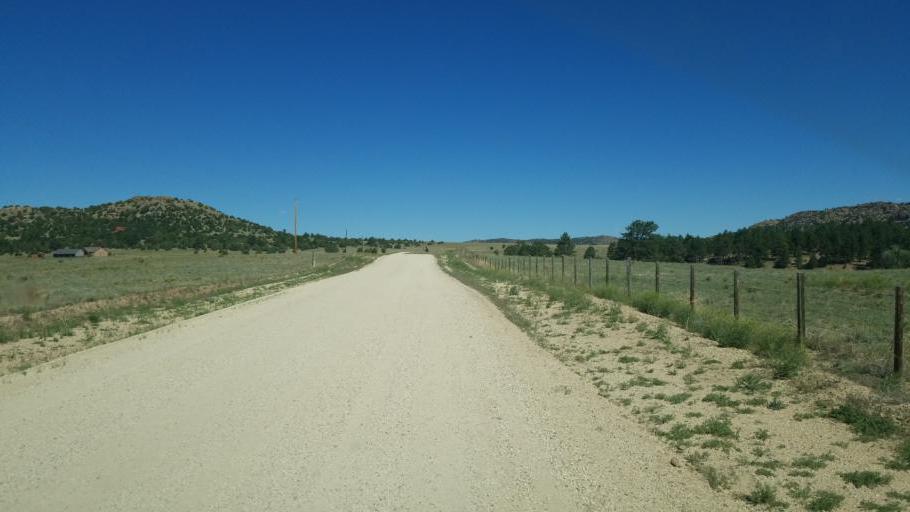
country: US
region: Colorado
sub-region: Custer County
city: Westcliffe
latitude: 38.2177
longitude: -105.4511
